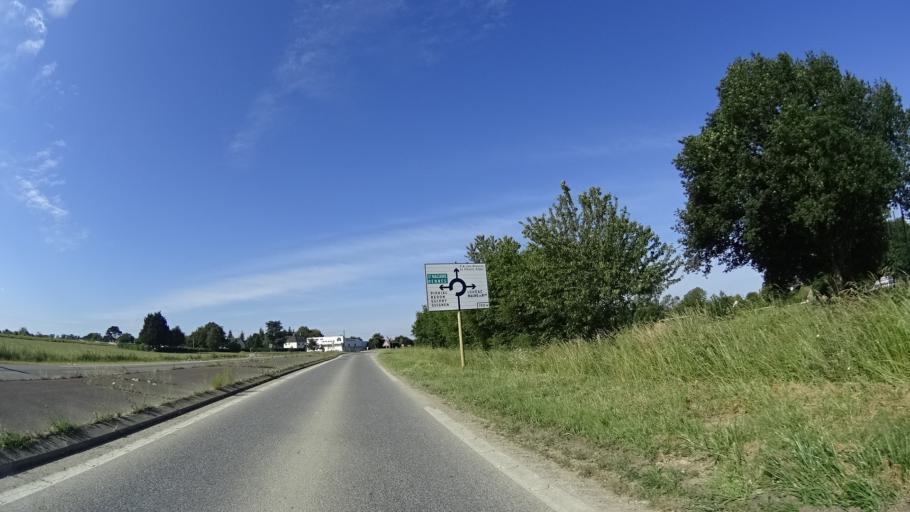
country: FR
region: Brittany
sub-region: Departement d'Ille-et-Vilaine
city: Guipry
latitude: 47.8641
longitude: -1.8795
